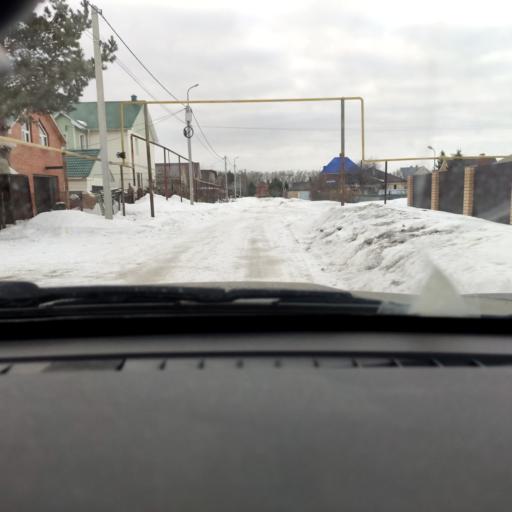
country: RU
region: Samara
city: Tol'yatti
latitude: 53.5521
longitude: 49.4005
